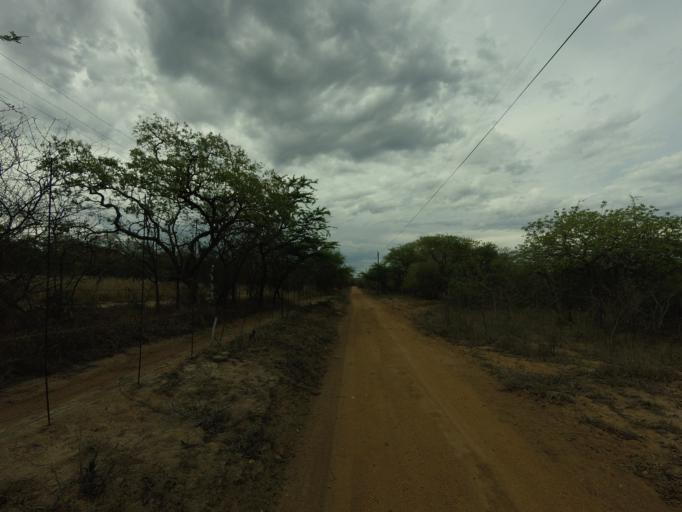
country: ZA
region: Limpopo
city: Thulamahashi
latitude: -24.5248
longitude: 31.1103
